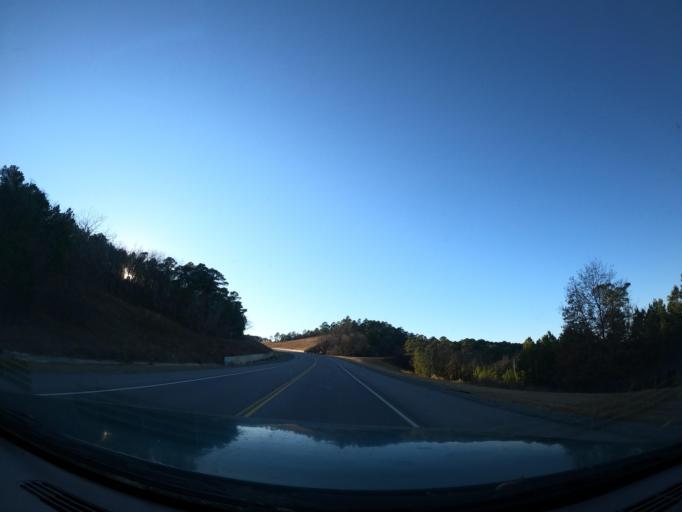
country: US
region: Oklahoma
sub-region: Pittsburg County
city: Hartshorne
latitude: 34.8913
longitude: -95.4534
